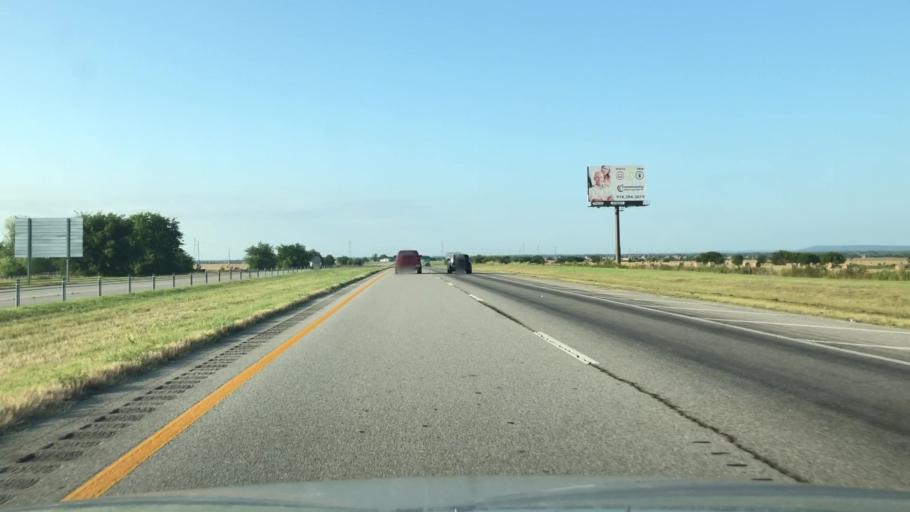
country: US
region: Oklahoma
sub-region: Osage County
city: Skiatook
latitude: 36.3609
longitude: -95.9208
